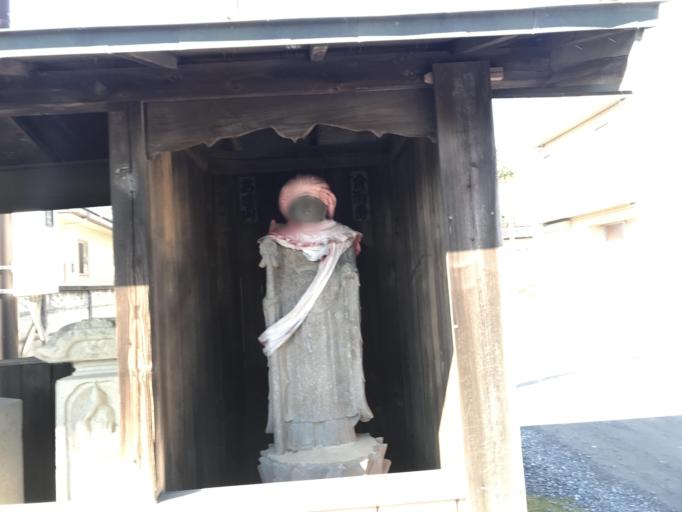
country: JP
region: Tochigi
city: Oyama
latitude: 36.2501
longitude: 139.8353
